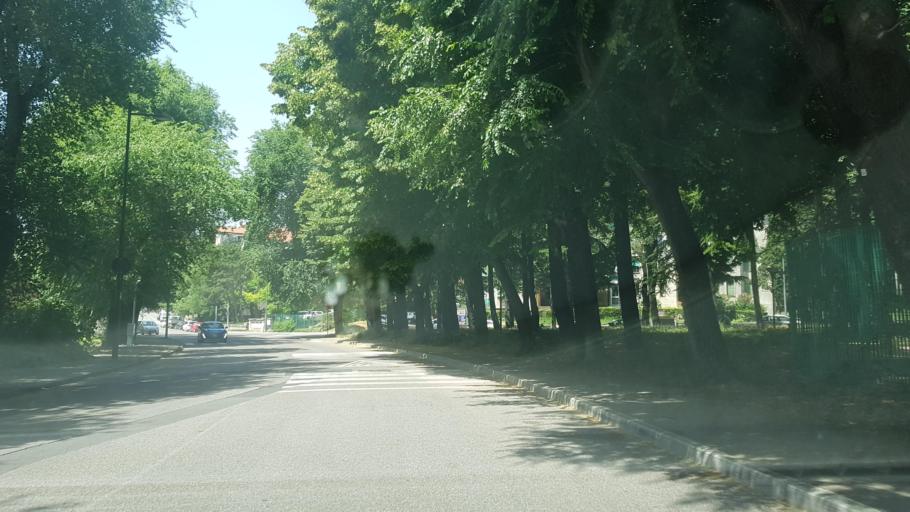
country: IT
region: Friuli Venezia Giulia
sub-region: Provincia di Trieste
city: Domio
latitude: 45.6183
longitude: 13.8211
